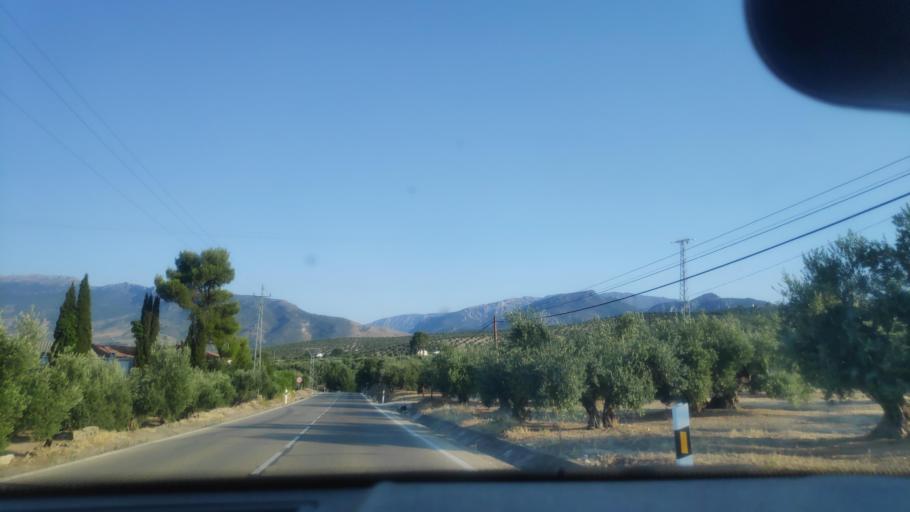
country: ES
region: Andalusia
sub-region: Provincia de Jaen
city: Jaen
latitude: 37.7401
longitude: -3.7740
